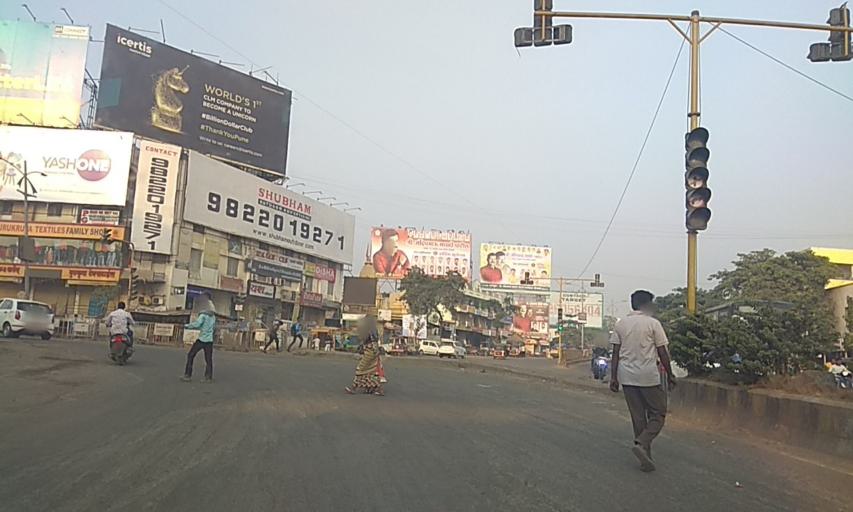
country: IN
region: Maharashtra
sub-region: Pune Division
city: Pimpri
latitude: 18.5912
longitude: 73.7392
